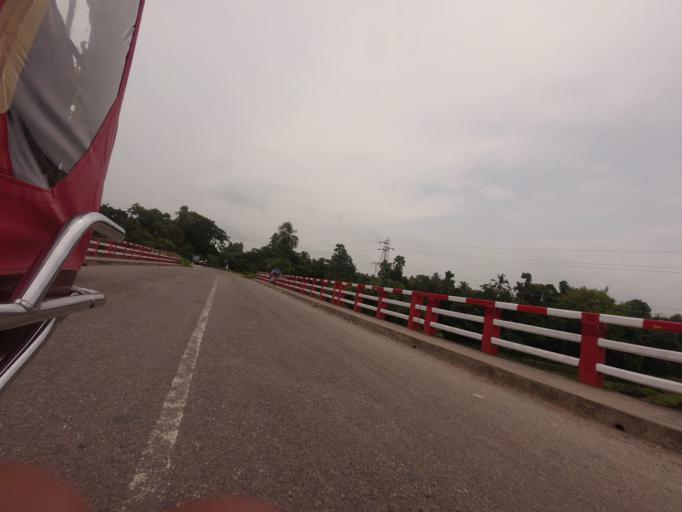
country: BD
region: Khulna
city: Kalia
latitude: 23.1829
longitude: 89.6528
